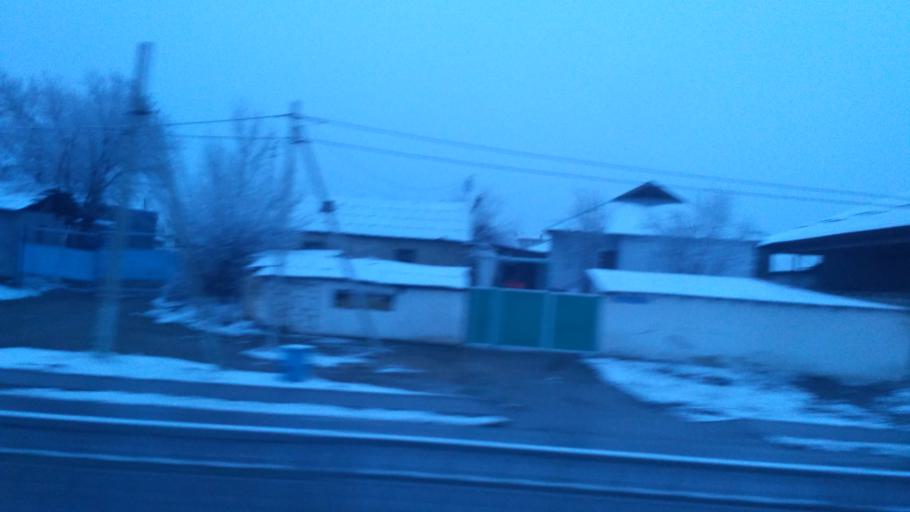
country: KZ
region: Ongtustik Qazaqstan
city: Shymkent
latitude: 42.3786
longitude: 69.4959
